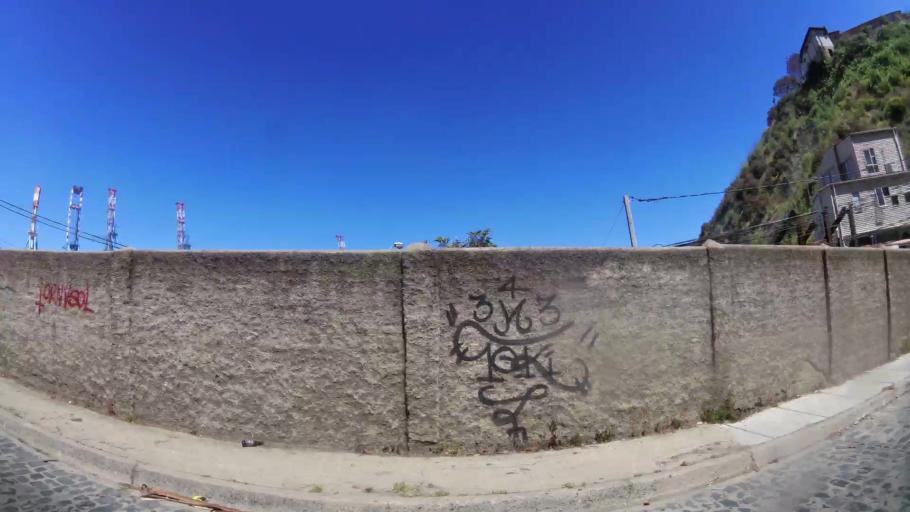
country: CL
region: Valparaiso
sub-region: Provincia de Valparaiso
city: Valparaiso
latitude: -33.0307
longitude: -71.6302
